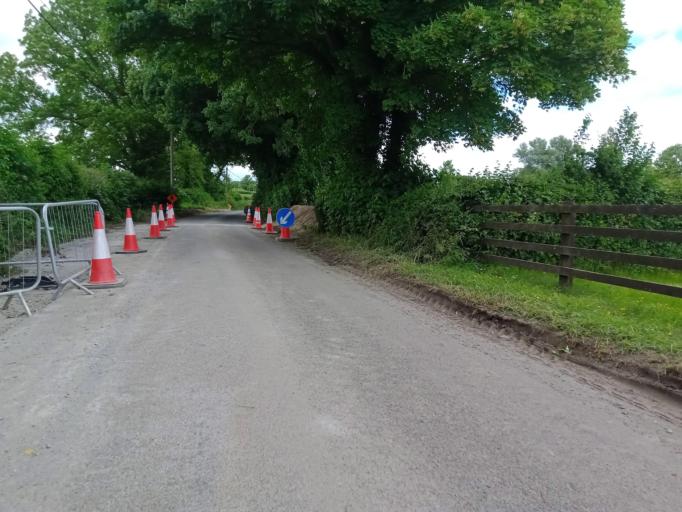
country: IE
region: Leinster
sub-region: Kilkenny
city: Kilkenny
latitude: 52.6863
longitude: -7.2493
